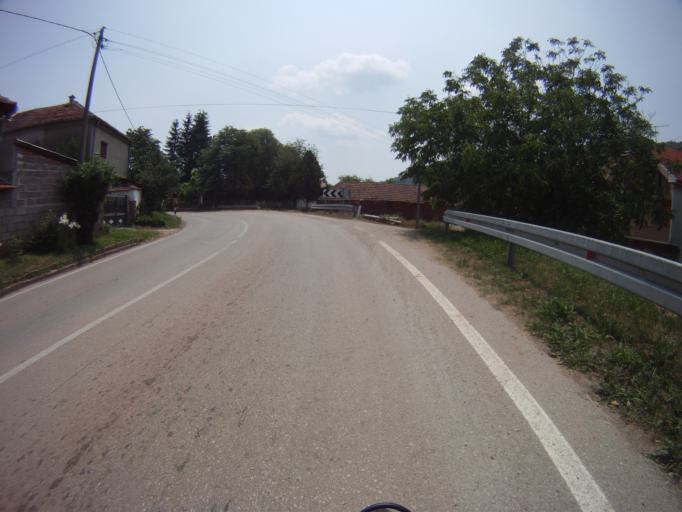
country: RS
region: Central Serbia
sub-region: Nisavski Okrug
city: Gadzin Han
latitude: 43.2403
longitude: 22.0151
